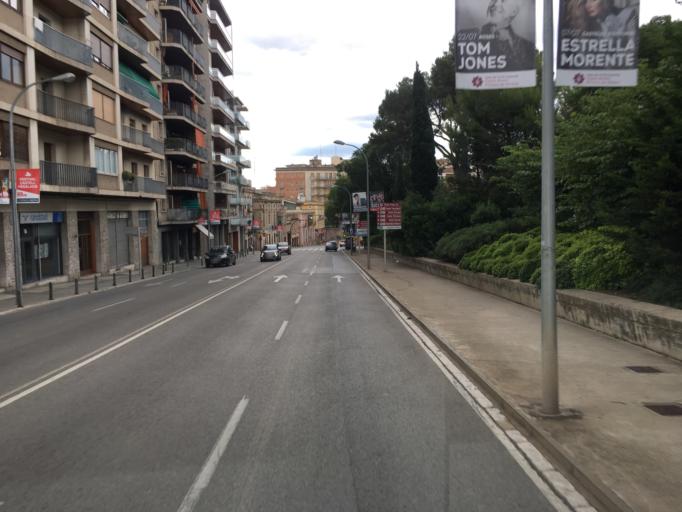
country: ES
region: Catalonia
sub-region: Provincia de Girona
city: Figueres
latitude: 42.2677
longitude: 2.9578
